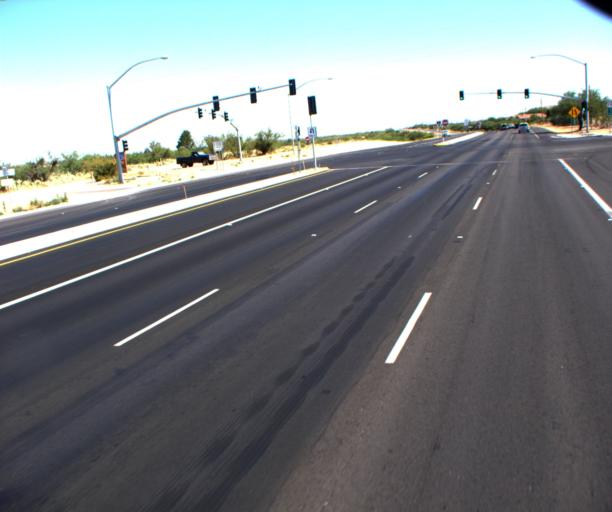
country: US
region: Arizona
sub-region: Pima County
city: Catalina
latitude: 32.5108
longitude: -110.9256
